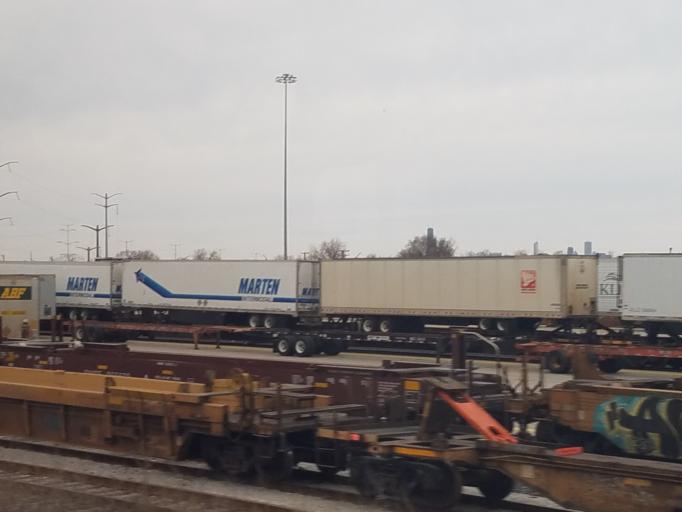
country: US
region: Illinois
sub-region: Cook County
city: Chicago
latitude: 41.7805
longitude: -87.6217
